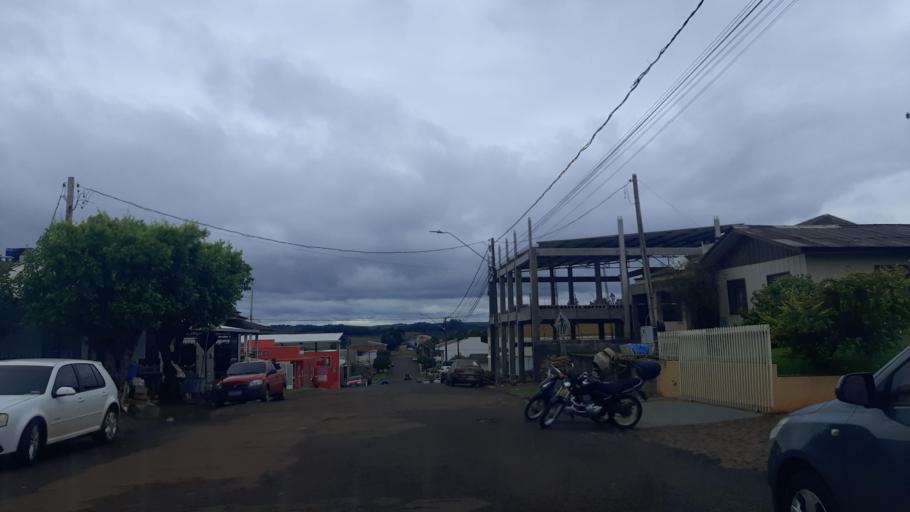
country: BR
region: Parana
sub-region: Ampere
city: Ampere
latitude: -25.9262
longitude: -53.4709
